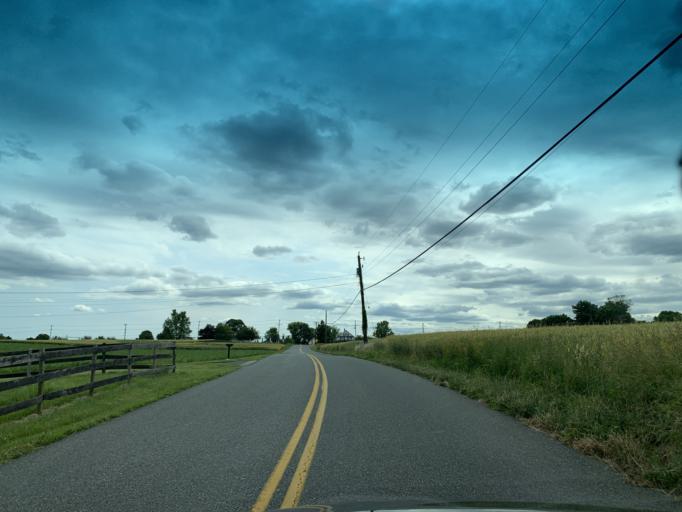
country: US
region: Maryland
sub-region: Harford County
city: Jarrettsville
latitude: 39.6129
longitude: -76.4987
